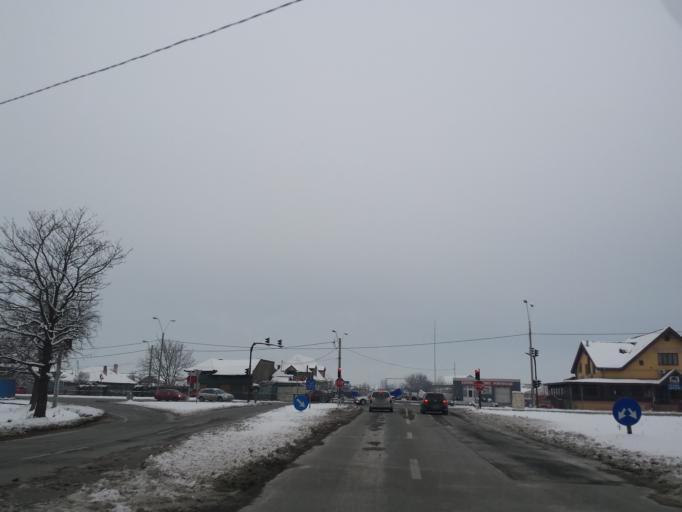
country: RO
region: Hunedoara
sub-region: Municipiul Deva
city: Cristur
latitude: 45.8554
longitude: 22.9552
